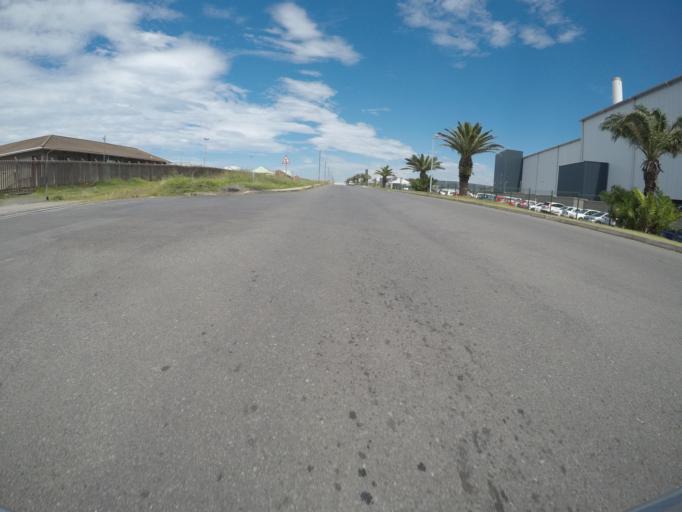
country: ZA
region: Eastern Cape
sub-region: Buffalo City Metropolitan Municipality
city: East London
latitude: -33.0297
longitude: 27.8992
